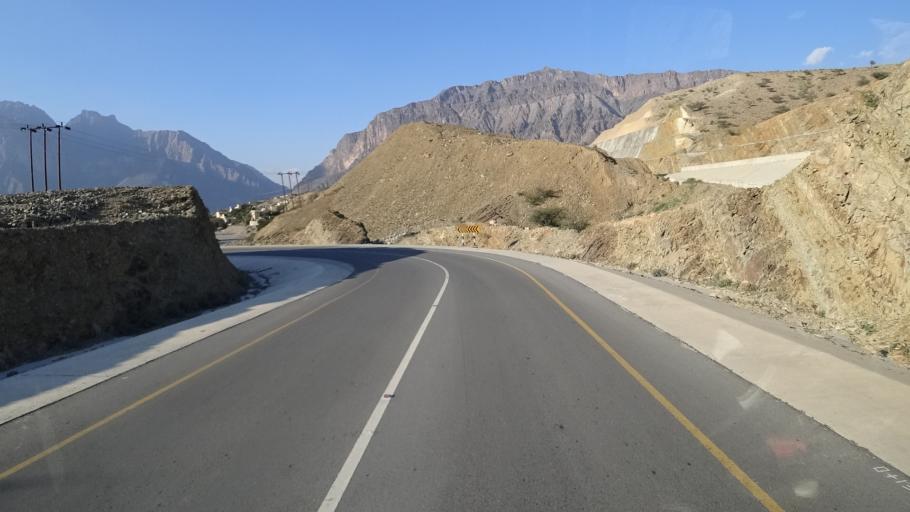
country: OM
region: Al Batinah
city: Rustaq
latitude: 23.2850
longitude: 57.3336
